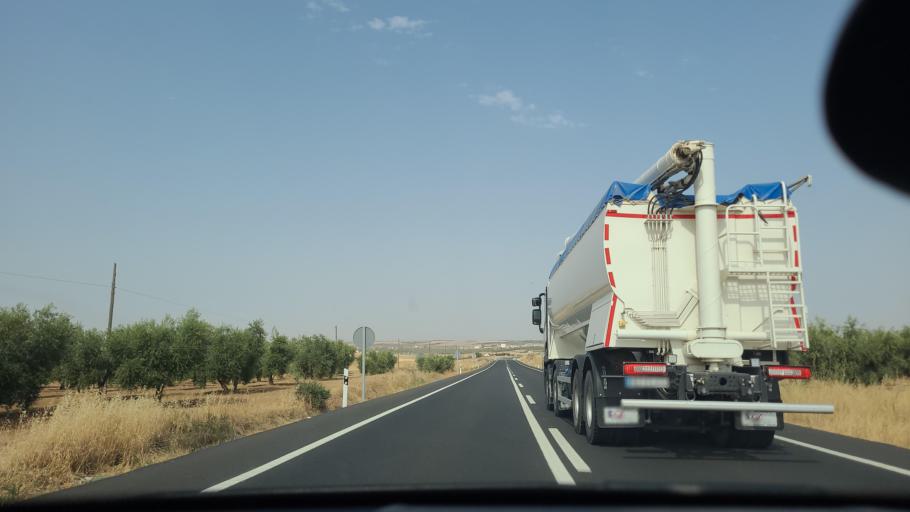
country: ES
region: Extremadura
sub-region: Provincia de Badajoz
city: Berlanga
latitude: 38.2667
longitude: -5.7824
